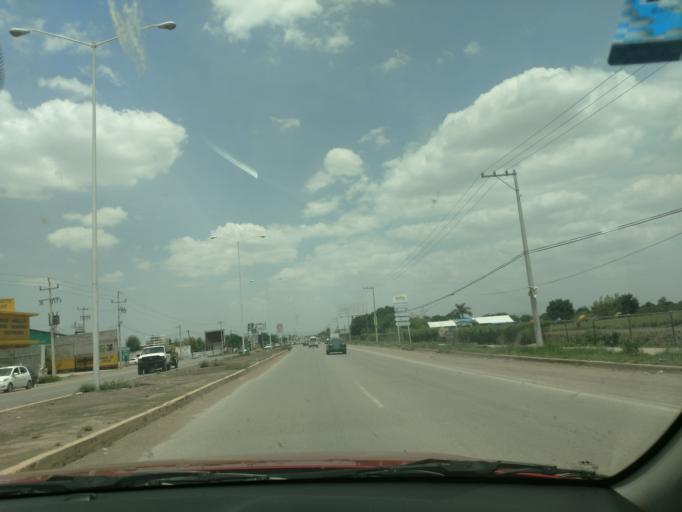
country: MX
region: San Luis Potosi
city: Ciudad Fernandez
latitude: 21.9364
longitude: -100.0287
